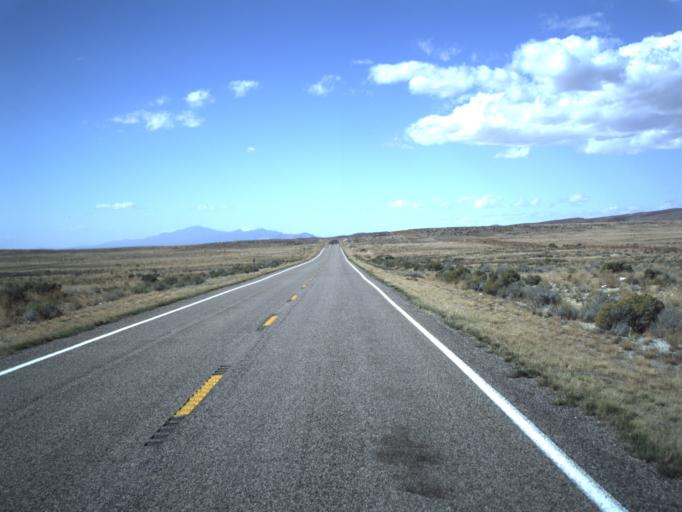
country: US
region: Utah
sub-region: Beaver County
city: Milford
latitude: 38.7965
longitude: -112.8991
